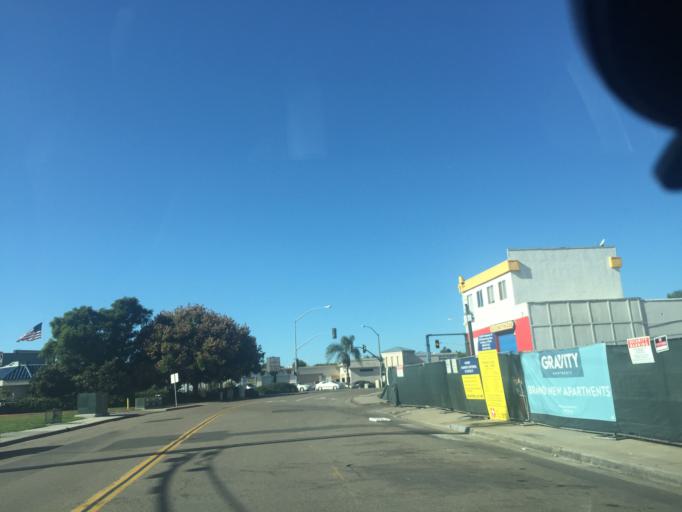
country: US
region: California
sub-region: San Diego County
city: La Mesa
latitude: 32.7830
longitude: -117.0974
